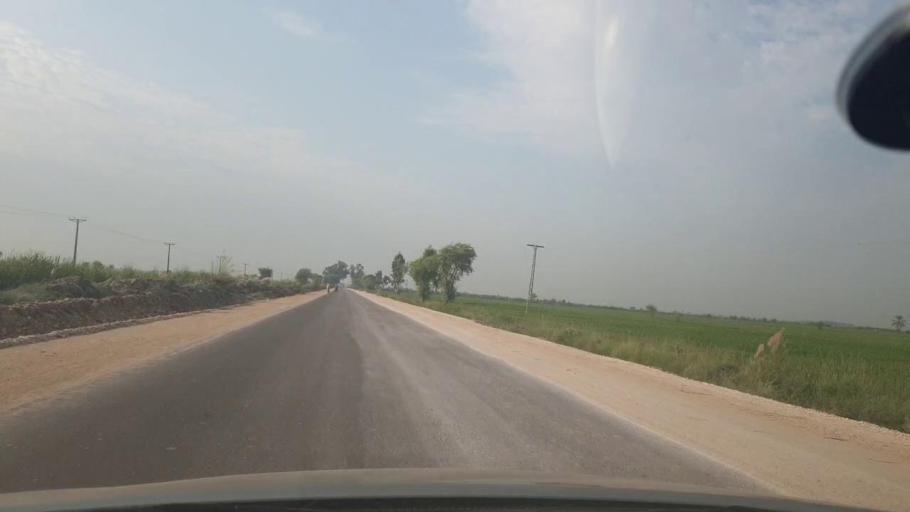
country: PK
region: Sindh
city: Jacobabad
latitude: 28.1886
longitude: 68.3675
